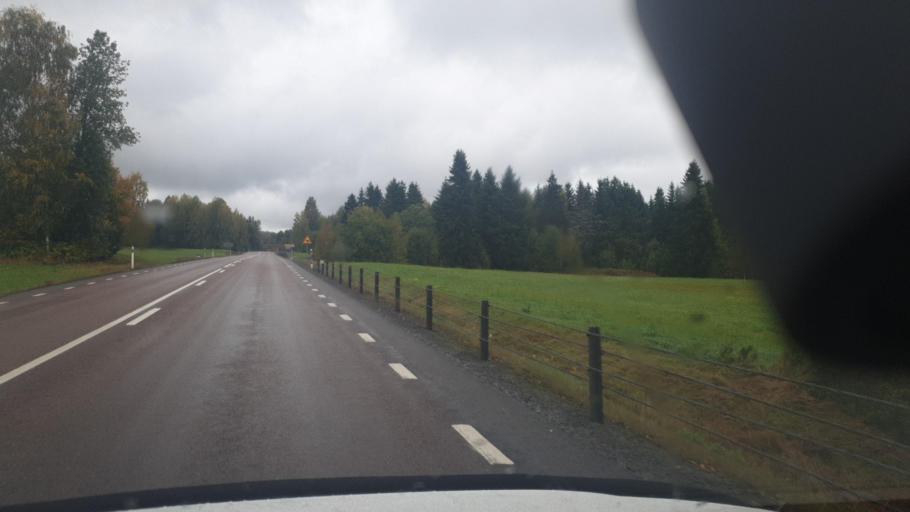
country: SE
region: Vaermland
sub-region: Sunne Kommun
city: Sunne
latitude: 59.7847
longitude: 13.0979
